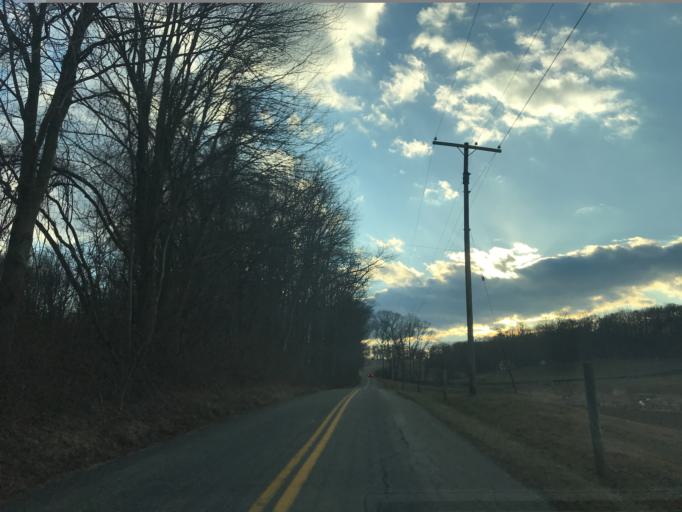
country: US
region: Maryland
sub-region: Harford County
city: Jarrettsville
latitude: 39.6080
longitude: -76.4259
